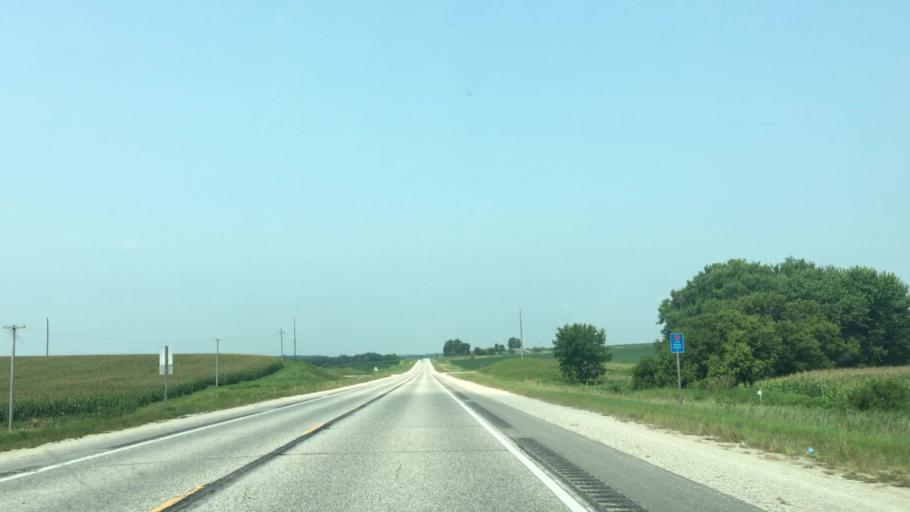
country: US
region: Iowa
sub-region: Fayette County
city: Fayette
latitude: 42.7863
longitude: -91.8048
